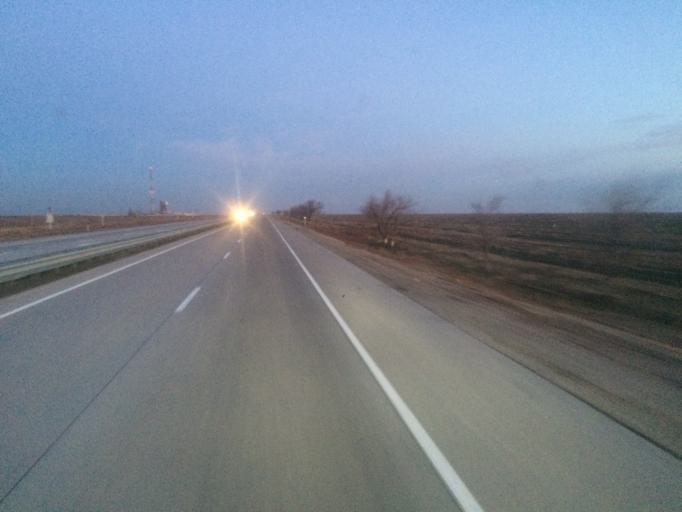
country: KZ
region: Ongtustik Qazaqstan
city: Temirlanovka
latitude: 42.8339
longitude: 69.1205
